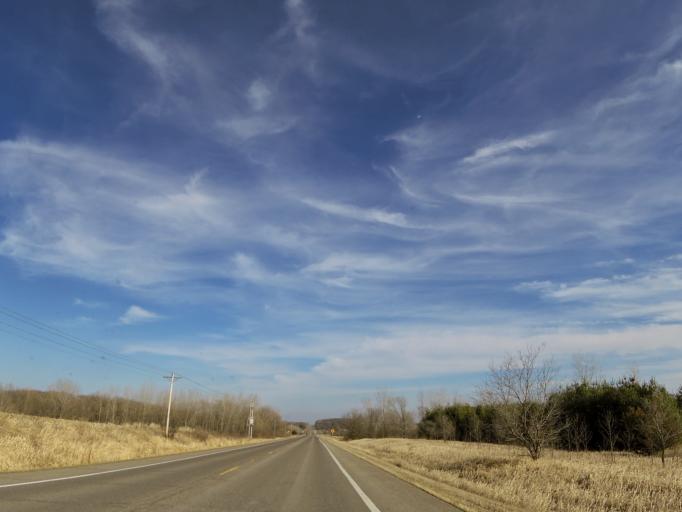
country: US
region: Minnesota
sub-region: Scott County
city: Elko New Market
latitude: 44.5439
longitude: -93.2455
